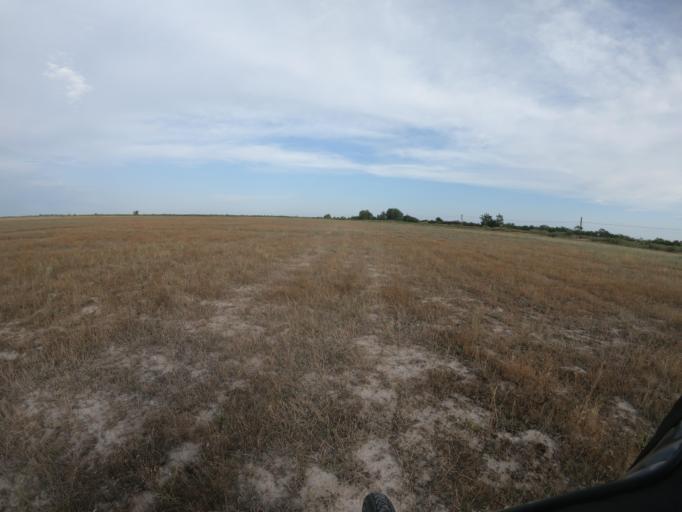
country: HU
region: Hajdu-Bihar
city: Hortobagy
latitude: 47.6072
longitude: 21.0543
